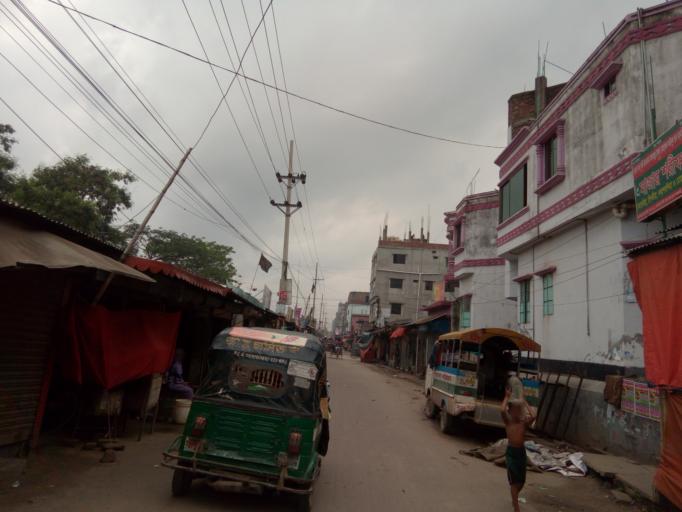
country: BD
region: Dhaka
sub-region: Dhaka
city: Dhaka
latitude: 23.6873
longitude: 90.4405
